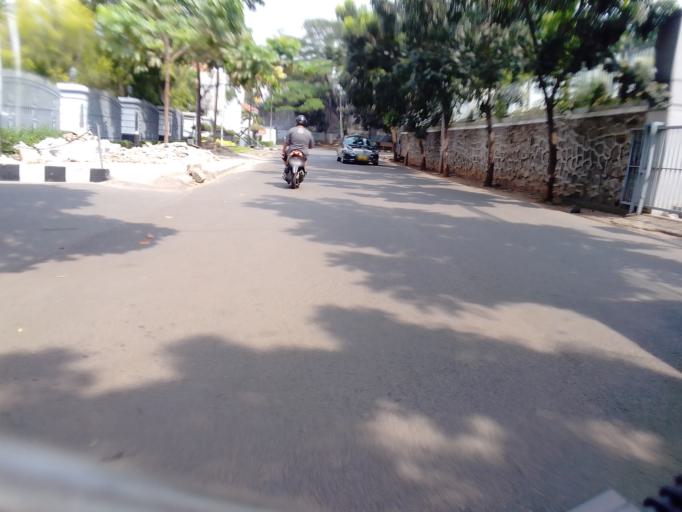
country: ID
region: Jakarta Raya
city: Jakarta
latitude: -6.2115
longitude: 106.8081
